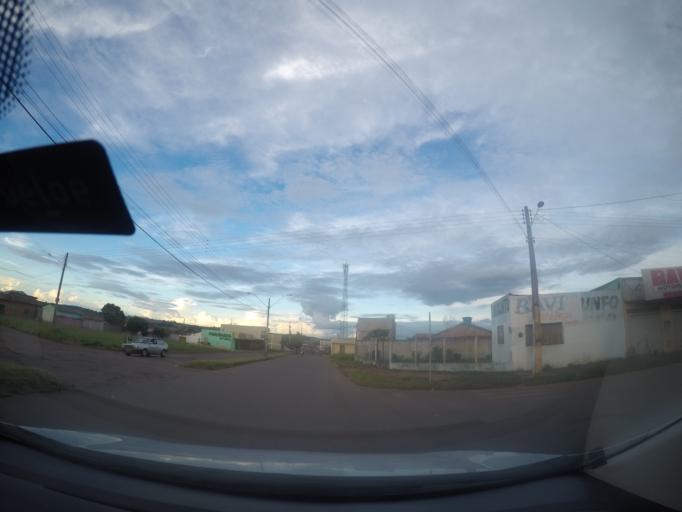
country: BR
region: Goias
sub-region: Goianira
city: Goianira
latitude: -16.5742
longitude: -49.3833
